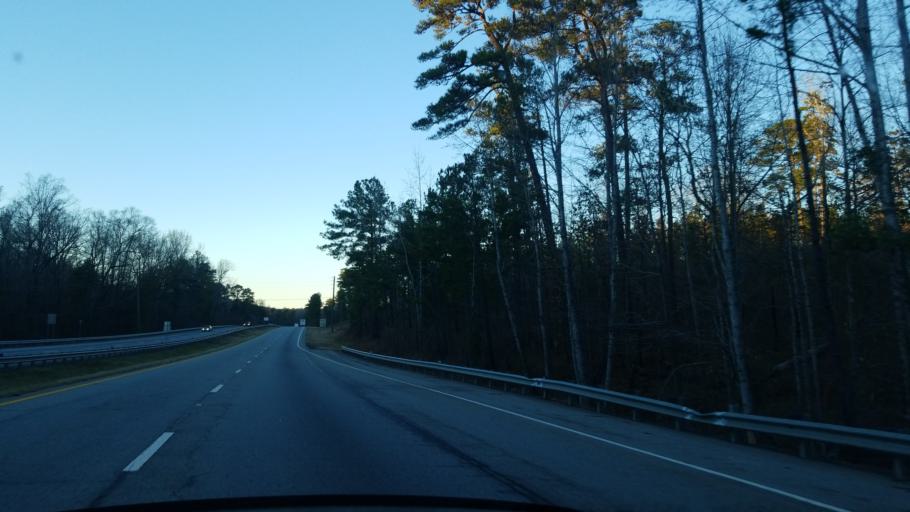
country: US
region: Georgia
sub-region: Chattahoochee County
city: Cusseta
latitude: 32.3163
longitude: -84.8006
